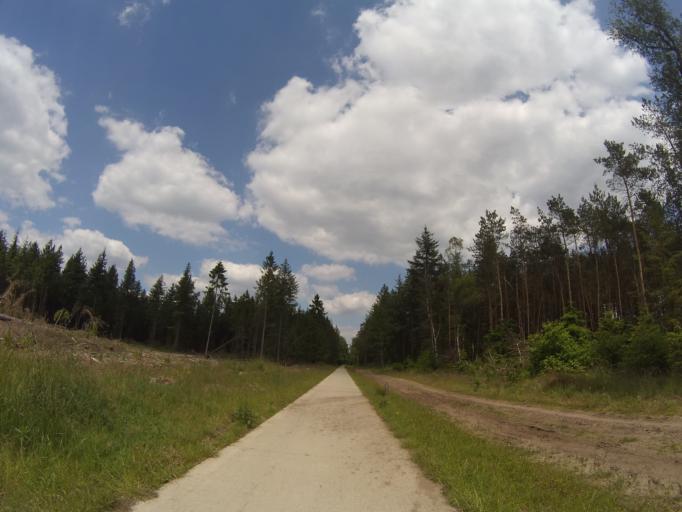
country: NL
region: Gelderland
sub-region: Gemeente Ede
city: Harskamp
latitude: 52.1747
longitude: 5.7615
